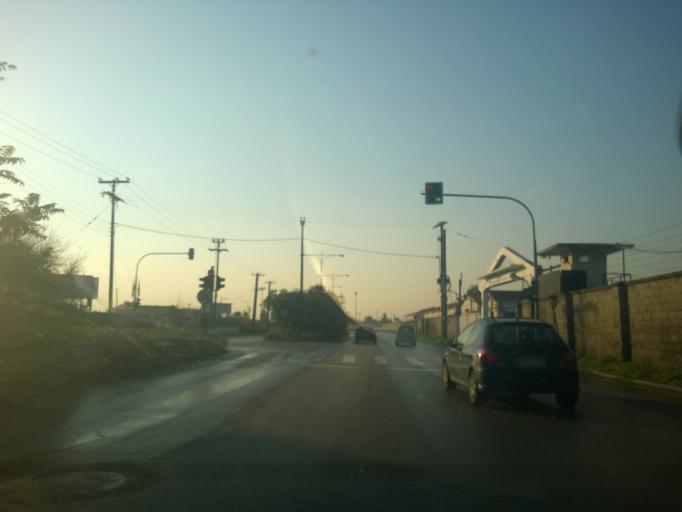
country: GR
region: Central Macedonia
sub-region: Nomos Thessalonikis
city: Menemeni
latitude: 40.6505
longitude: 22.9021
